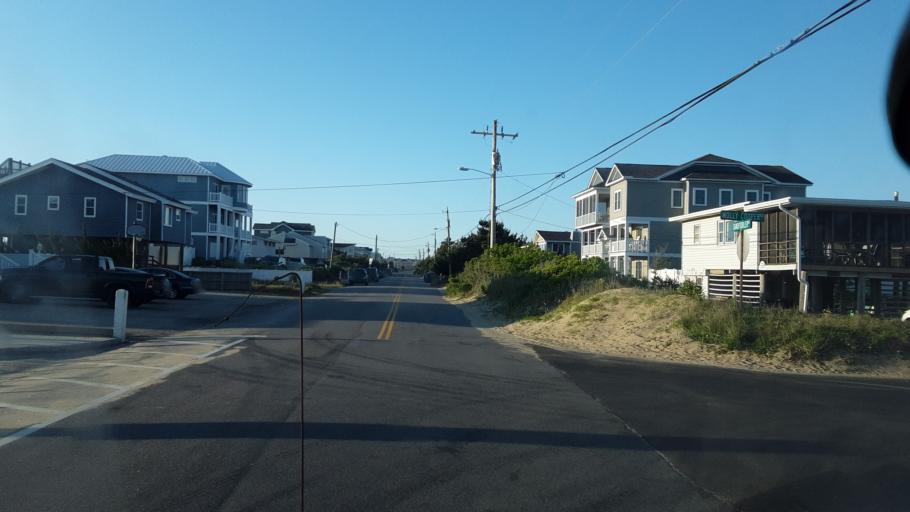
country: US
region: Virginia
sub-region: City of Virginia Beach
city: Virginia Beach
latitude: 36.7089
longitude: -75.9303
